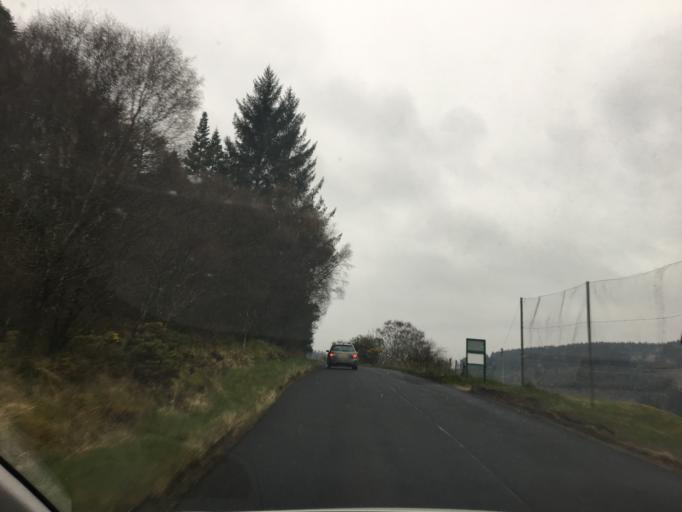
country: GB
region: Scotland
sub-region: North Ayrshire
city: Lamlash
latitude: 55.5450
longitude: -5.1325
